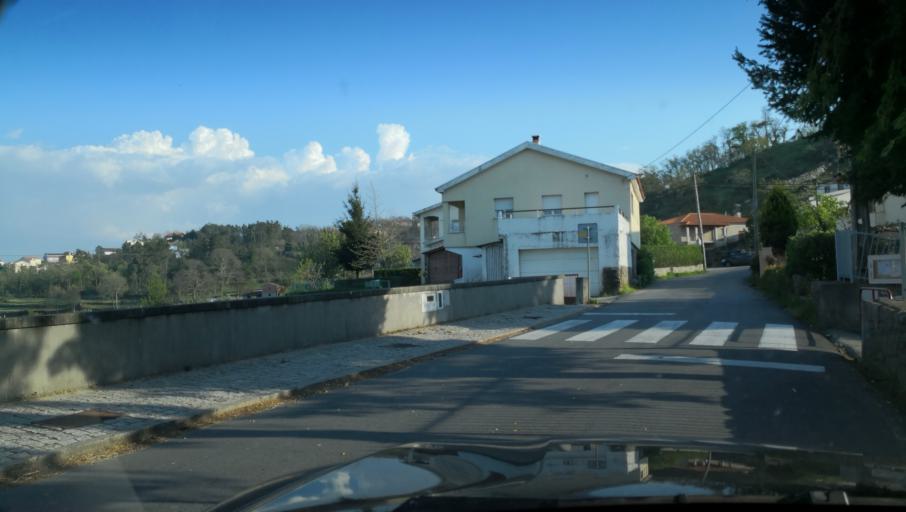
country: PT
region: Vila Real
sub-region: Santa Marta de Penaguiao
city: Santa Marta de Penaguiao
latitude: 41.2805
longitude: -7.8142
